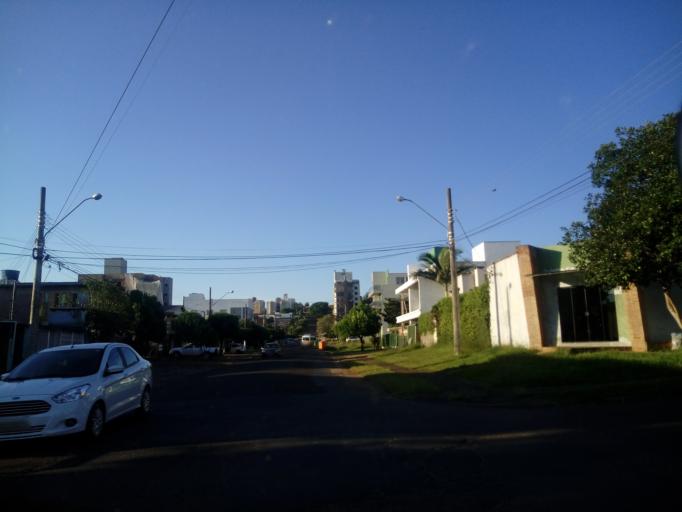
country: BR
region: Santa Catarina
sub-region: Chapeco
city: Chapeco
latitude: -27.1105
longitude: -52.6077
